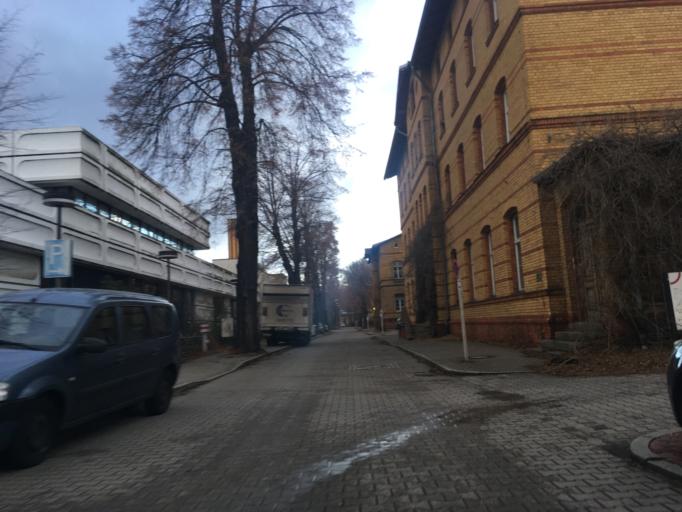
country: DE
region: Berlin
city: Wittenau
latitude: 52.5814
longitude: 13.3297
